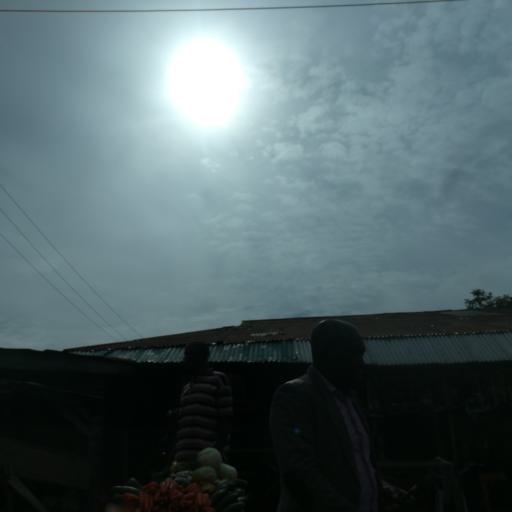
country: NG
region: Lagos
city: Oshodi
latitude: 6.5558
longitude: 3.3490
